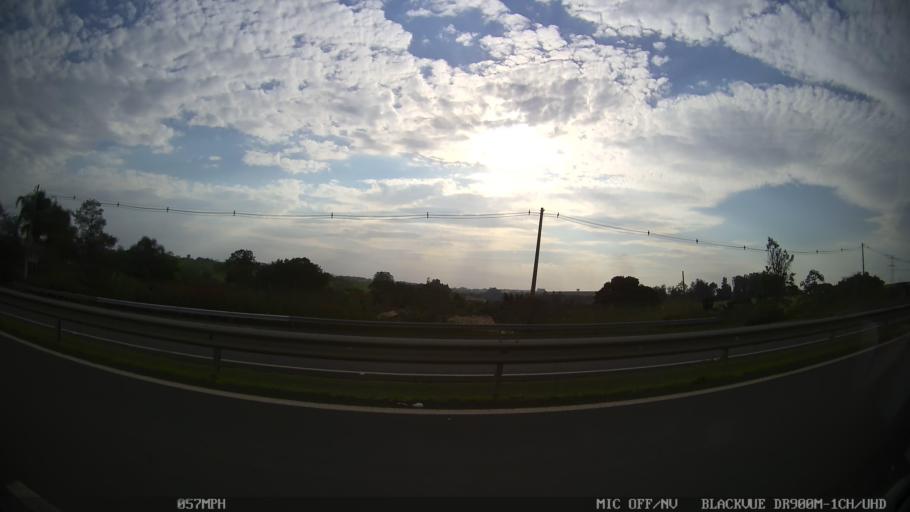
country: BR
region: Sao Paulo
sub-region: Cosmopolis
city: Cosmopolis
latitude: -22.6119
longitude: -47.1951
